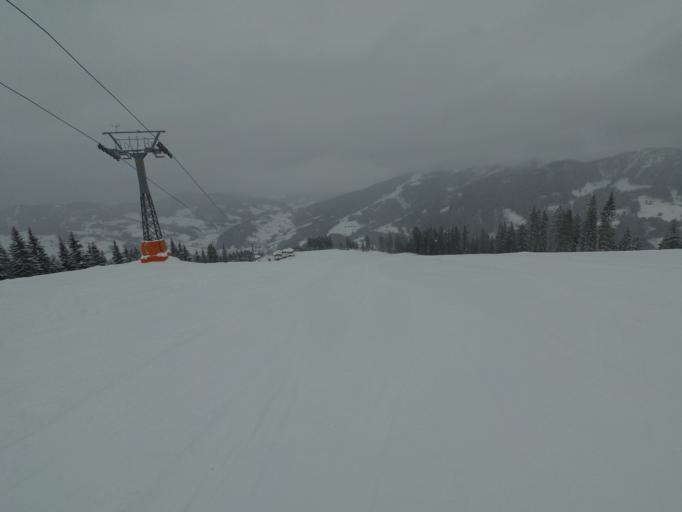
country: AT
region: Salzburg
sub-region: Politischer Bezirk Sankt Johann im Pongau
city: Wagrain
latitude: 47.3127
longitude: 13.2790
